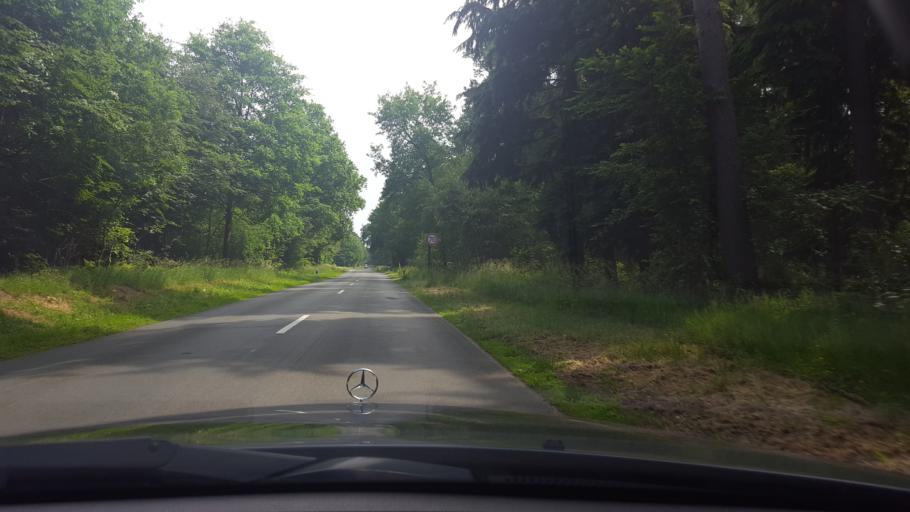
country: DE
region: North Rhine-Westphalia
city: Olfen
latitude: 51.7182
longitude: 7.3069
